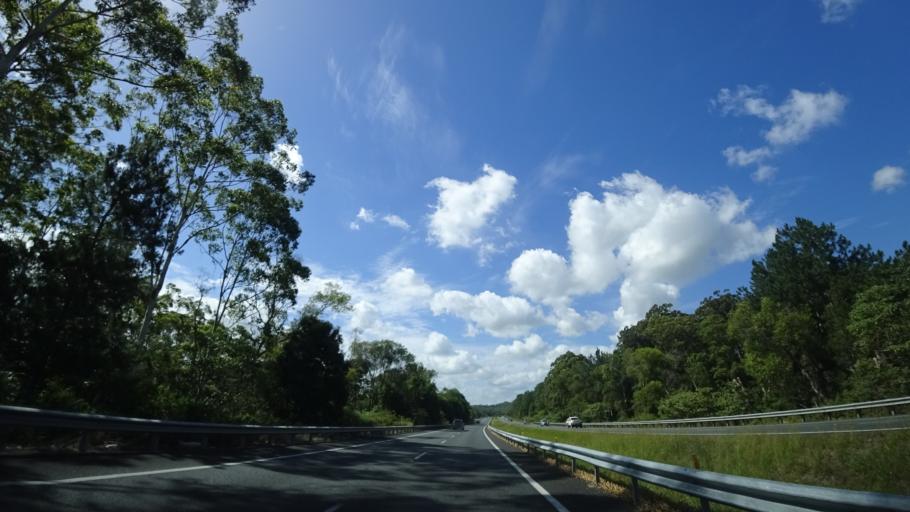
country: AU
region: Queensland
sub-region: Sunshine Coast
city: Woombye
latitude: -26.6500
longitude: 152.9896
